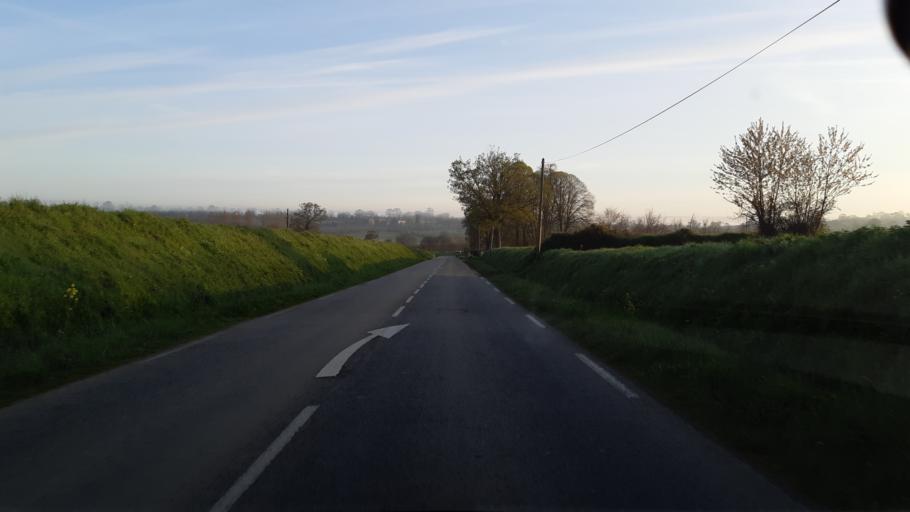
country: FR
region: Lower Normandy
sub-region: Departement de la Manche
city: Agneaux
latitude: 49.0626
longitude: -1.1328
